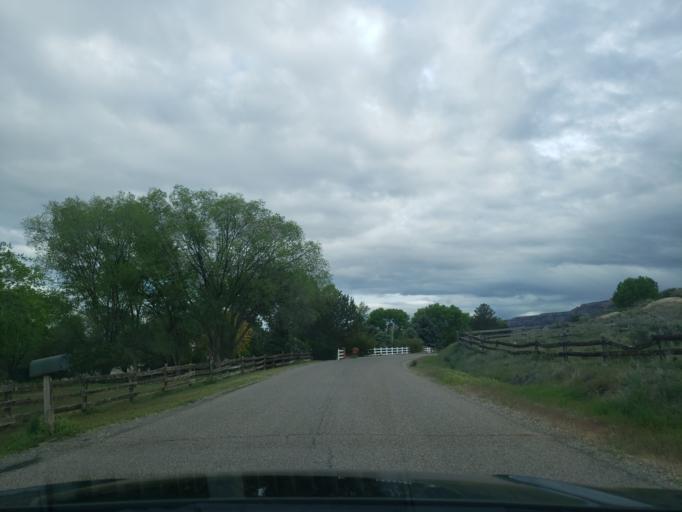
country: US
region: Colorado
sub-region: Mesa County
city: Redlands
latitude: 39.1044
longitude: -108.6802
